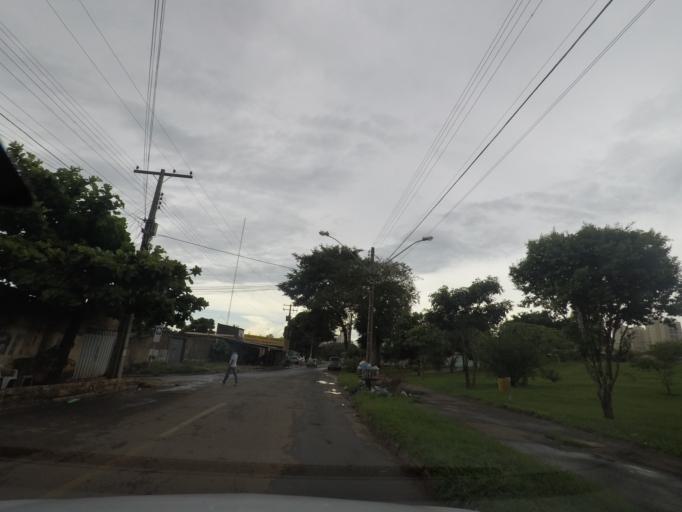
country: BR
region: Goias
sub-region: Goiania
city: Goiania
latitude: -16.7183
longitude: -49.2455
